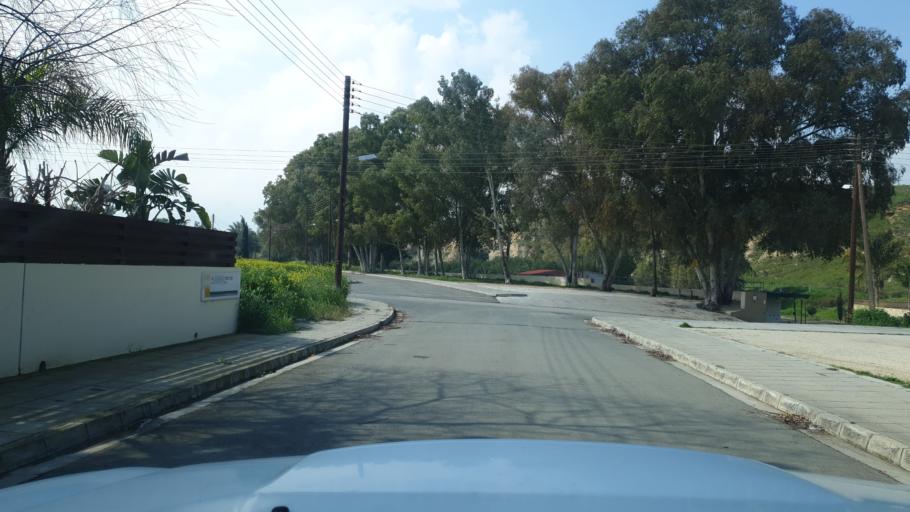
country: CY
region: Lefkosia
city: Kato Deftera
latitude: 35.0910
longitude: 33.2828
